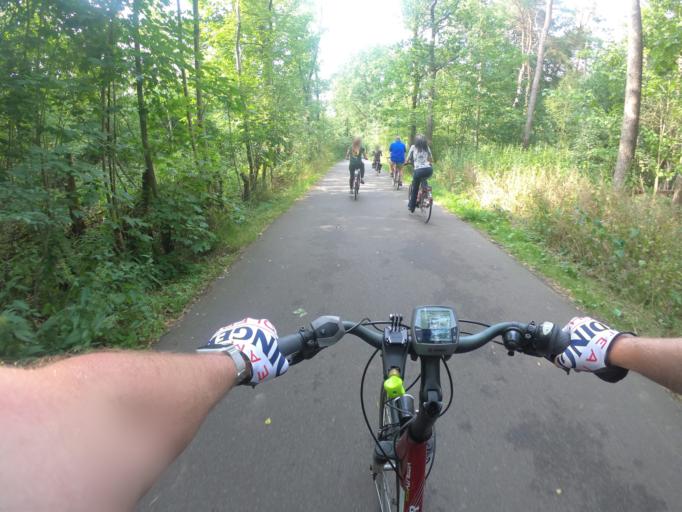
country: NL
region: Gelderland
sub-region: Gemeente Nijmegen
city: Nijmegen
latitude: 51.7919
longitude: 5.8594
